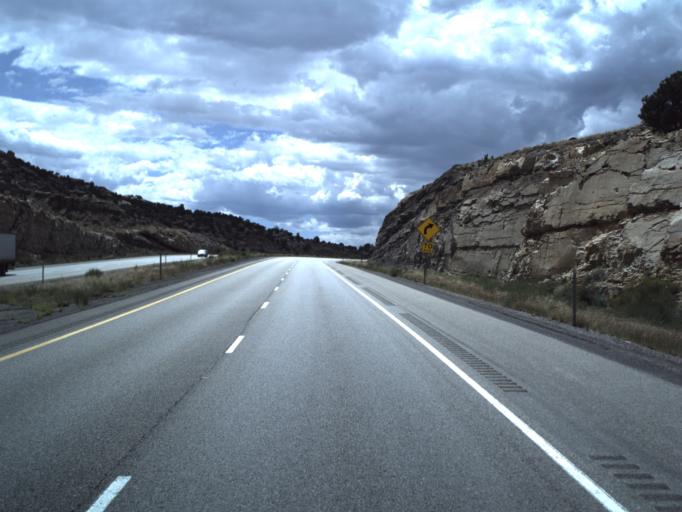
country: US
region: Utah
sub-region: Emery County
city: Ferron
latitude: 38.8033
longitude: -111.2652
